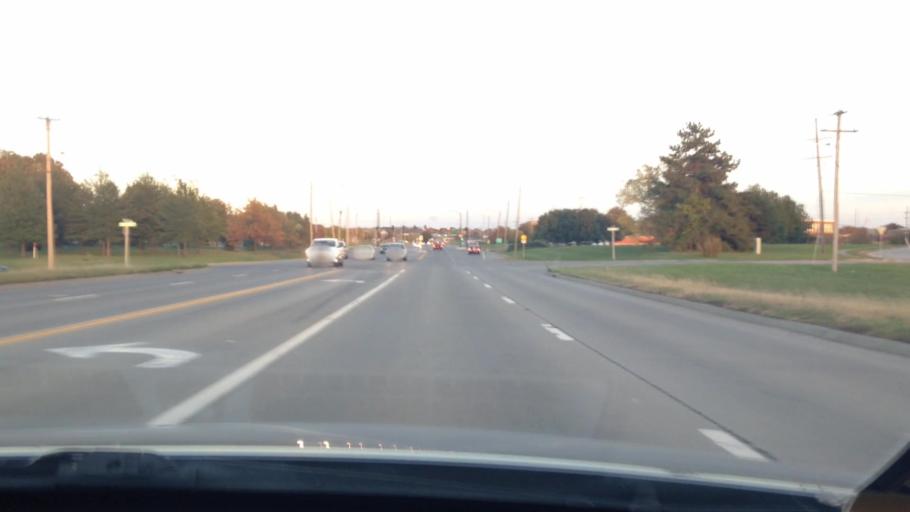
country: US
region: Kansas
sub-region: Johnson County
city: Olathe
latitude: 38.8676
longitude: -94.8194
